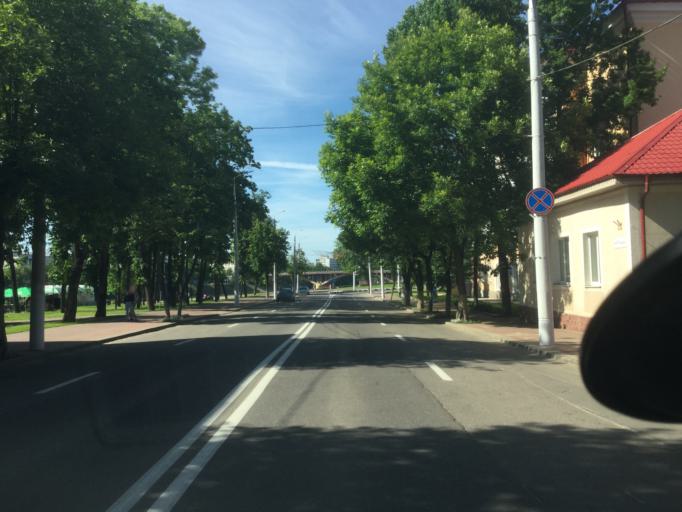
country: BY
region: Vitebsk
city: Vitebsk
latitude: 55.1888
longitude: 30.2009
